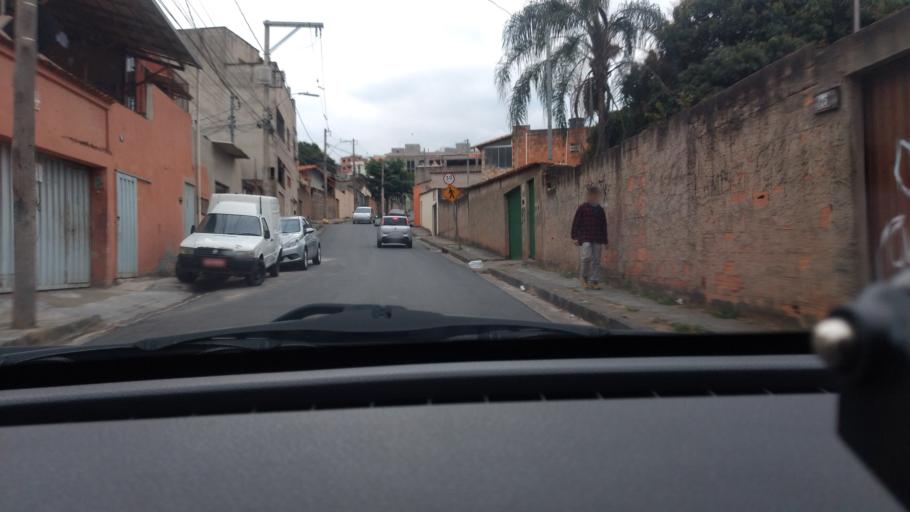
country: BR
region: Minas Gerais
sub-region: Santa Luzia
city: Santa Luzia
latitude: -19.8207
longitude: -43.9374
